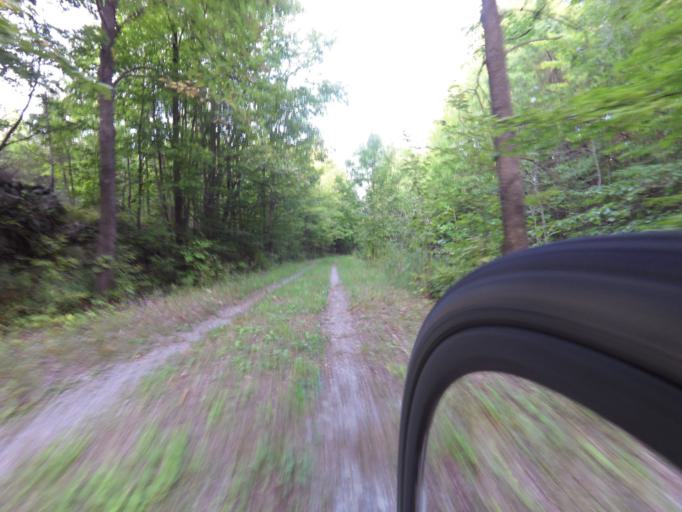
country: CA
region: Ontario
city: Gananoque
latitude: 44.5761
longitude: -76.3347
